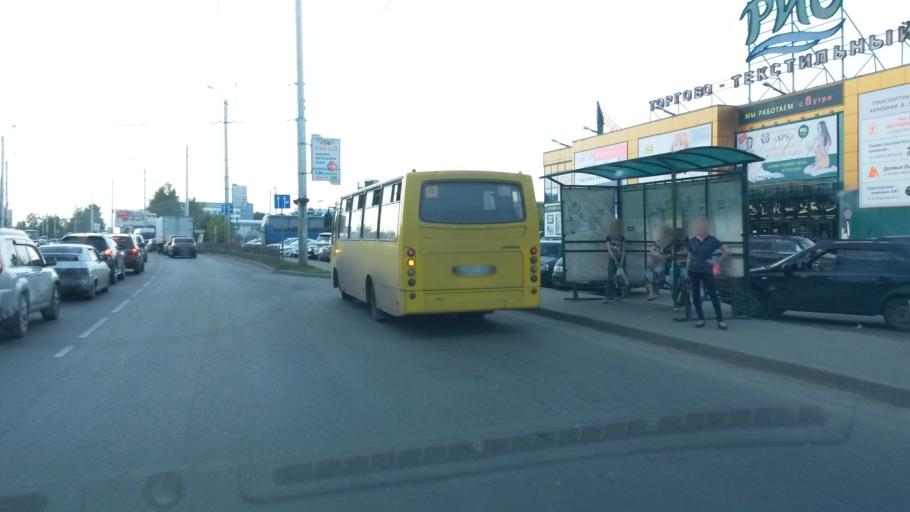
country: RU
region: Ivanovo
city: Kokhma
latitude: 56.9564
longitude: 41.0397
